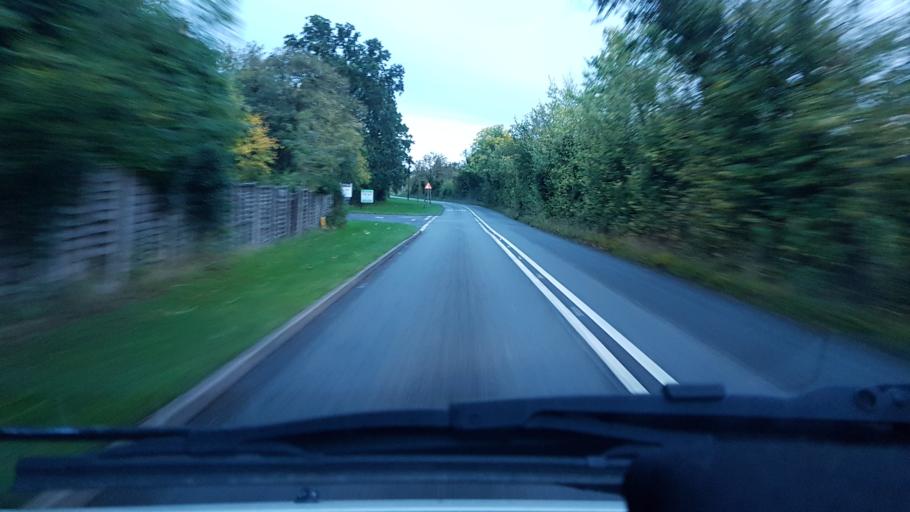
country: GB
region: England
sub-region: Worcestershire
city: Great Malvern
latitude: 52.0911
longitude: -2.3111
